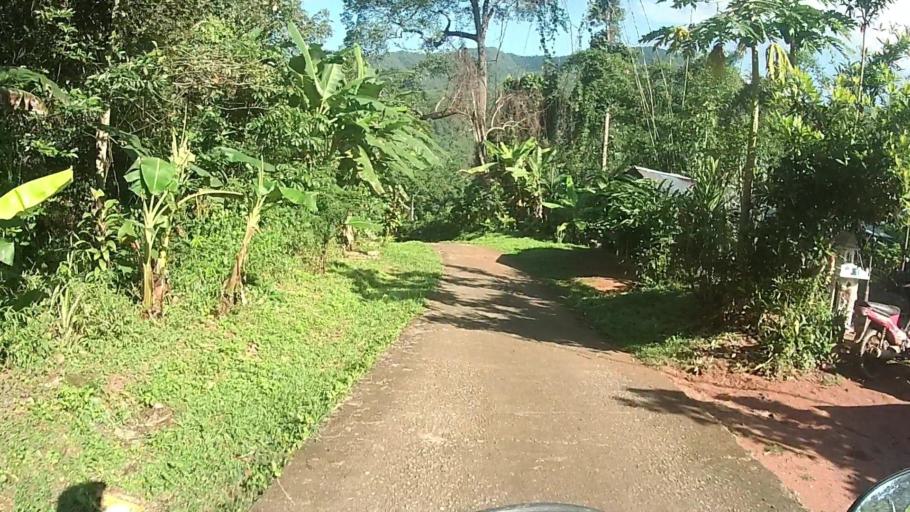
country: TH
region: Chiang Mai
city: Mae On
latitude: 18.9224
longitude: 99.2862
